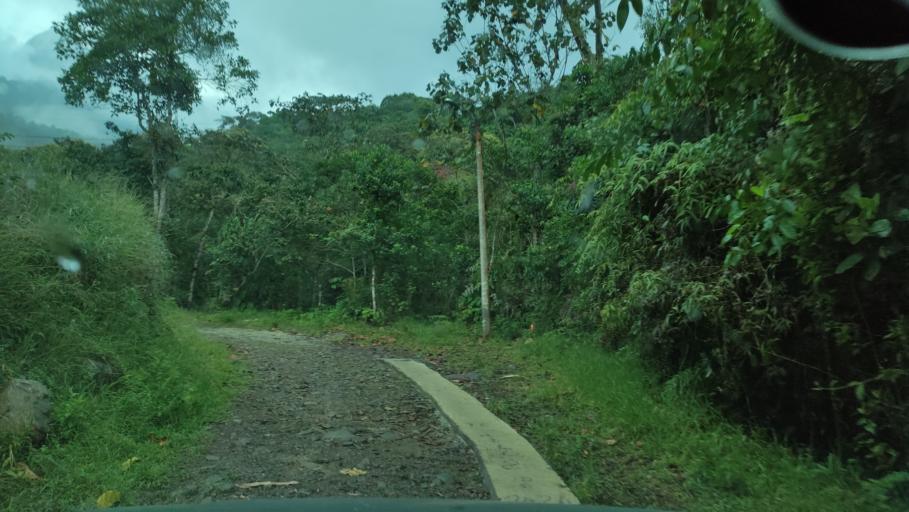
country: CO
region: Valle del Cauca
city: Jamundi
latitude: 3.3210
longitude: -76.6338
